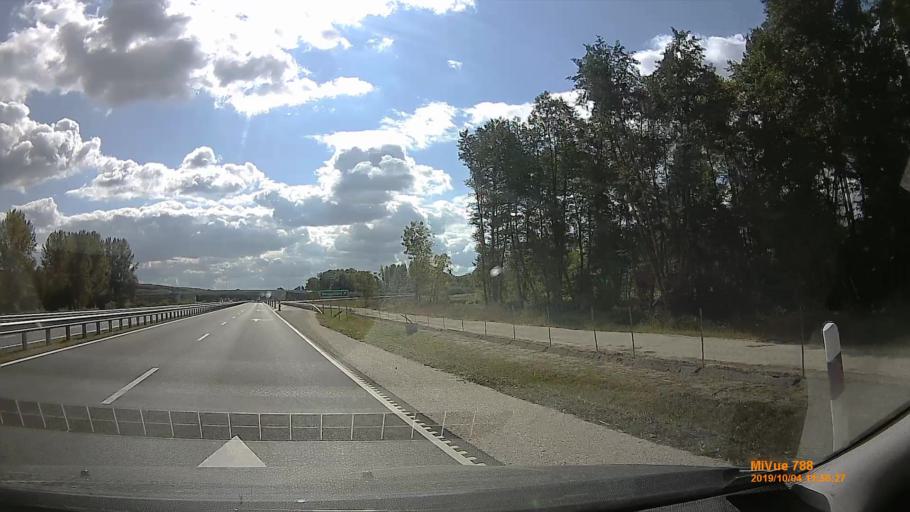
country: HU
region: Somogy
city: Karad
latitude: 46.6706
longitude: 17.7806
